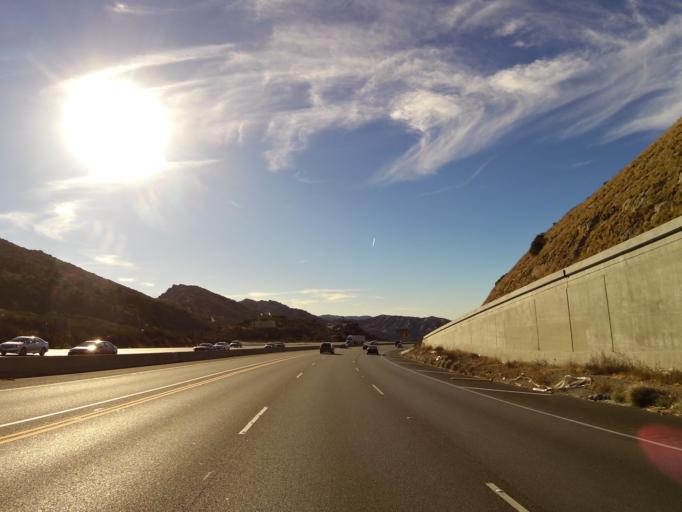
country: US
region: California
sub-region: Los Angeles County
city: Chatsworth
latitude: 34.2673
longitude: -118.6368
